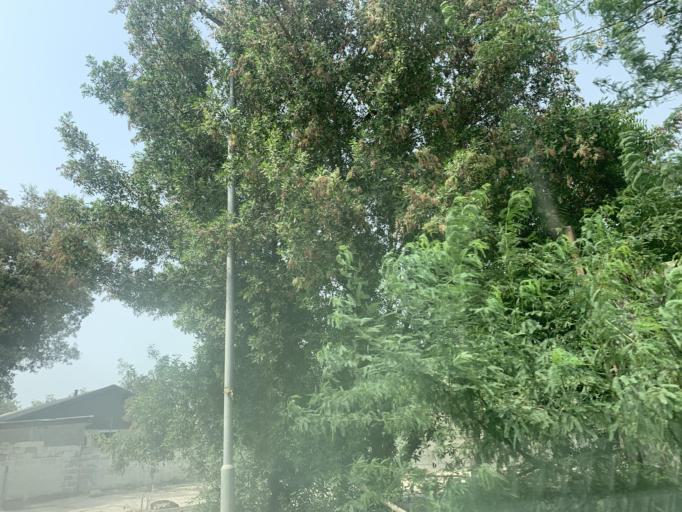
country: BH
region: Manama
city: Jidd Hafs
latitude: 26.2013
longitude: 50.4625
